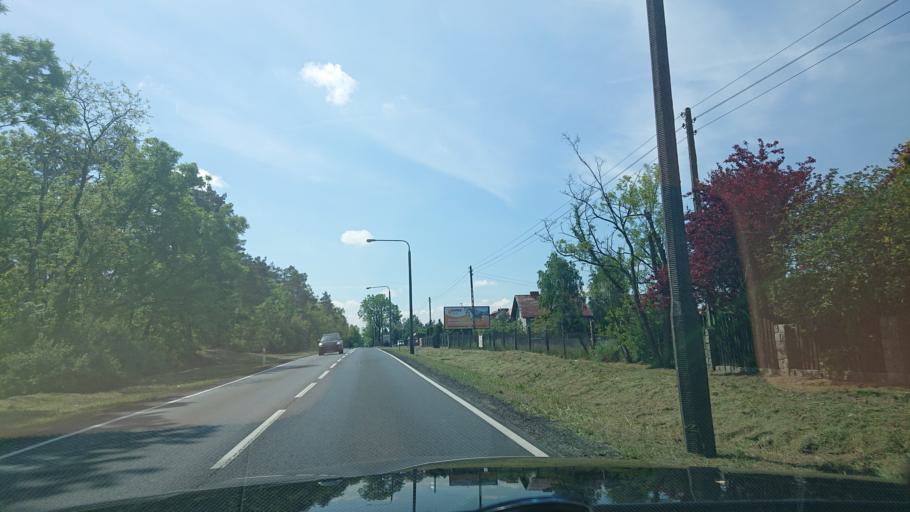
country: PL
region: Greater Poland Voivodeship
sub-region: Powiat gnieznienski
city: Gniezno
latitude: 52.5004
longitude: 17.5944
